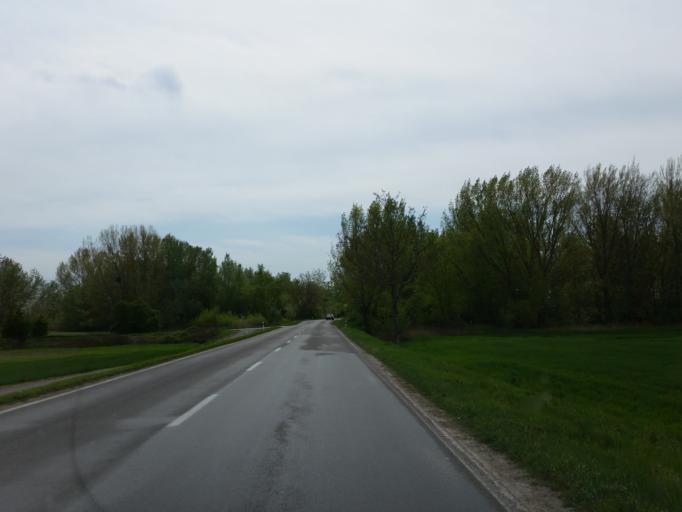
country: SK
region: Trnavsky
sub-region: Okres Dunajska Streda
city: Velky Meder
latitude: 47.8726
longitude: 17.7921
